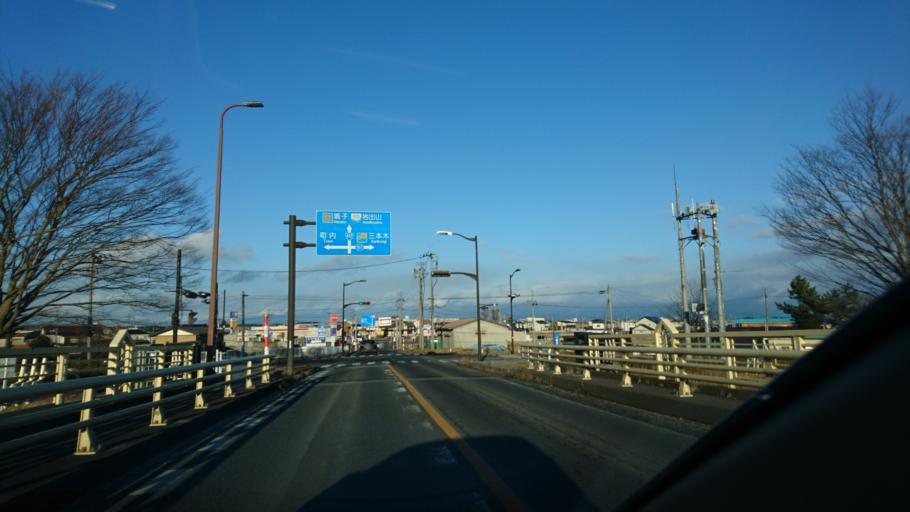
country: JP
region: Miyagi
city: Furukawa
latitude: 38.5593
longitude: 140.8588
